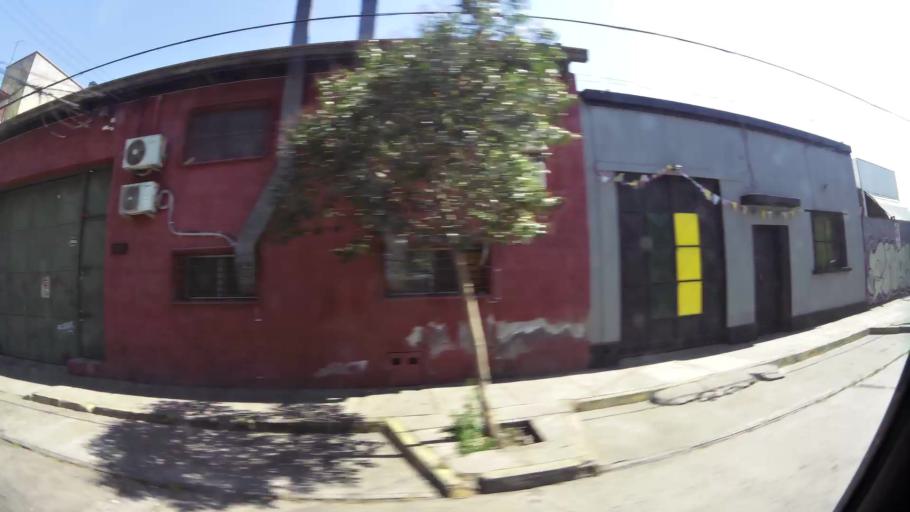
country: CL
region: Santiago Metropolitan
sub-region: Provincia de Santiago
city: Santiago
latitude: -33.4573
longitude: -70.6364
